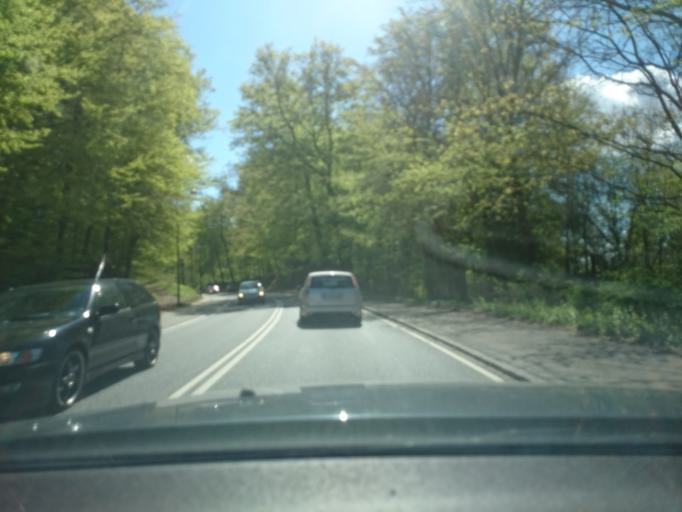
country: DK
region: Capital Region
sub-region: Gentofte Kommune
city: Charlottenlund
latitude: 55.7708
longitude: 12.5569
